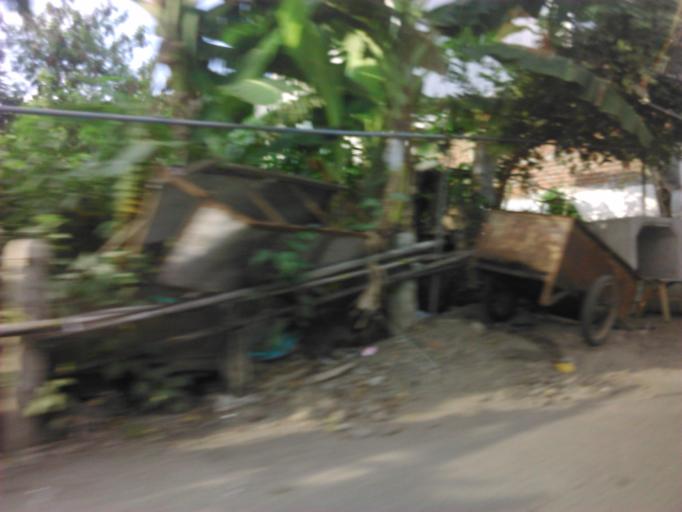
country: ID
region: East Java
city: Wonorejo
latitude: -7.2902
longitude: 112.7964
